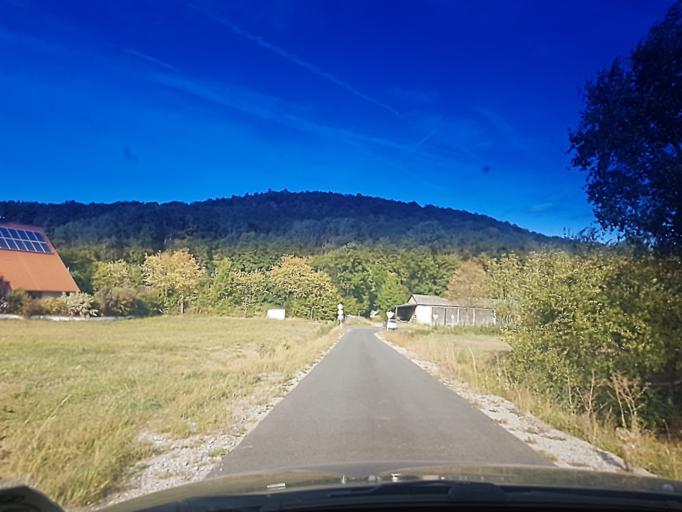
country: DE
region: Bavaria
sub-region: Upper Franconia
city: Schlusselfeld
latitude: 49.7726
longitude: 10.5804
